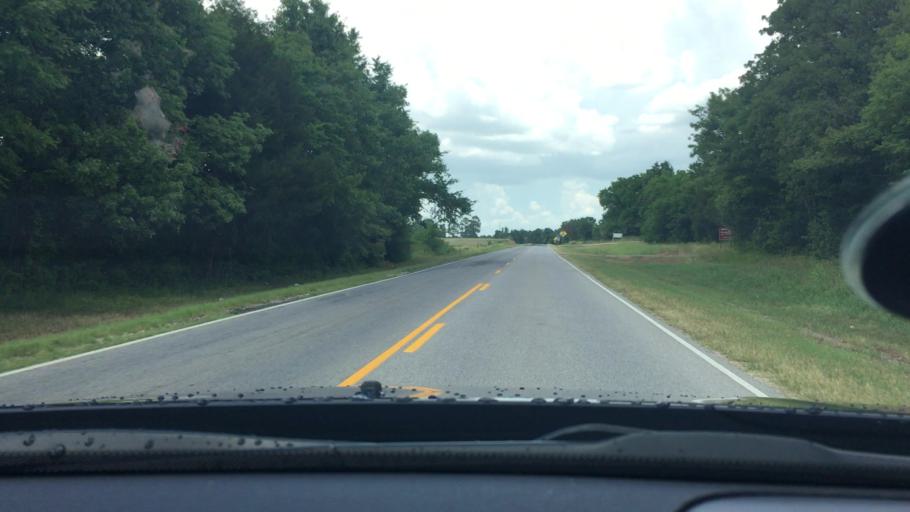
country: US
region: Oklahoma
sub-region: Johnston County
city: Tishomingo
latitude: 34.2244
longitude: -96.6995
